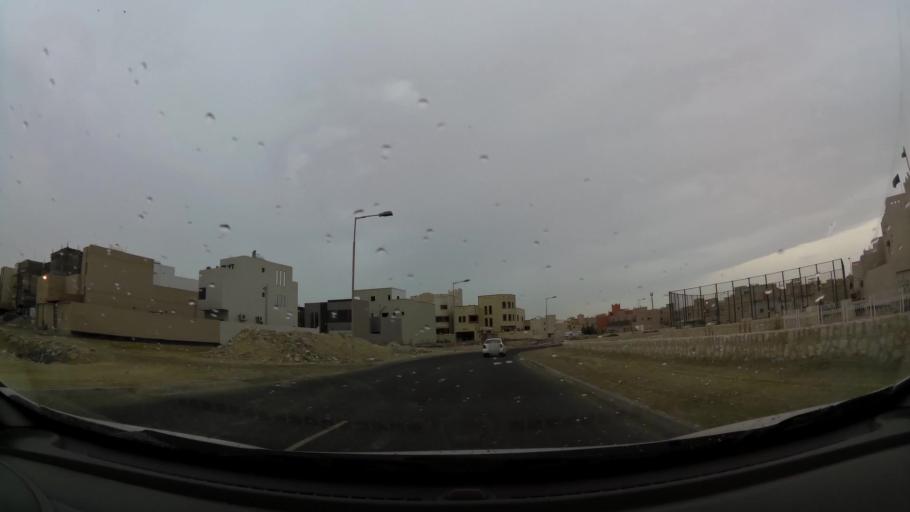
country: BH
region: Central Governorate
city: Madinat Hamad
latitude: 26.1274
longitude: 50.4877
